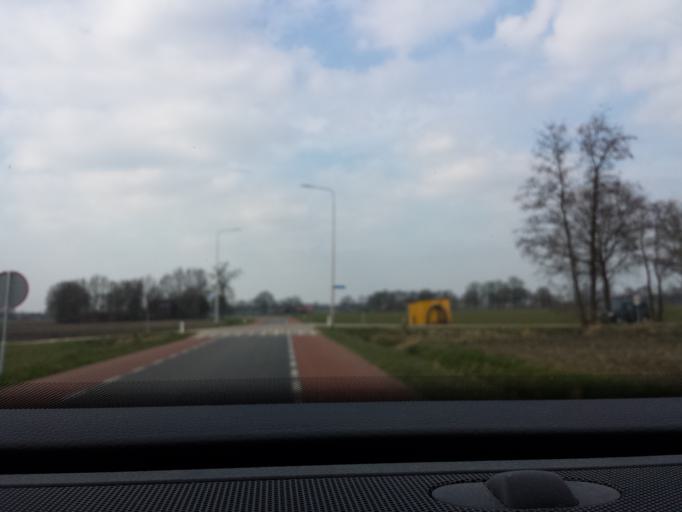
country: NL
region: Gelderland
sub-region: Gemeente Lochem
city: Barchem
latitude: 52.0580
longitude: 6.4682
